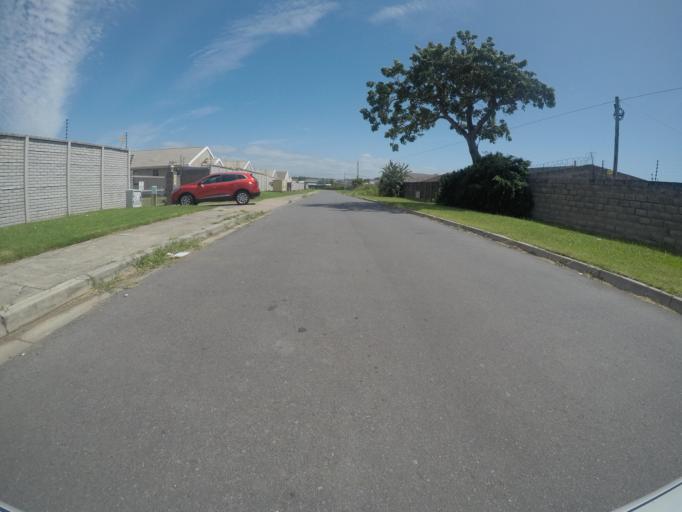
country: ZA
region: Eastern Cape
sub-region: Buffalo City Metropolitan Municipality
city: East London
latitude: -32.9520
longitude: 27.9961
